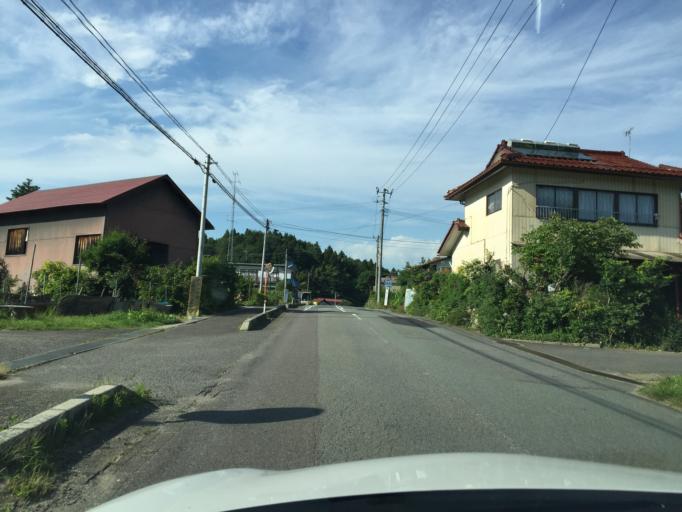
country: JP
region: Fukushima
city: Sukagawa
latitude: 37.3219
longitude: 140.4874
